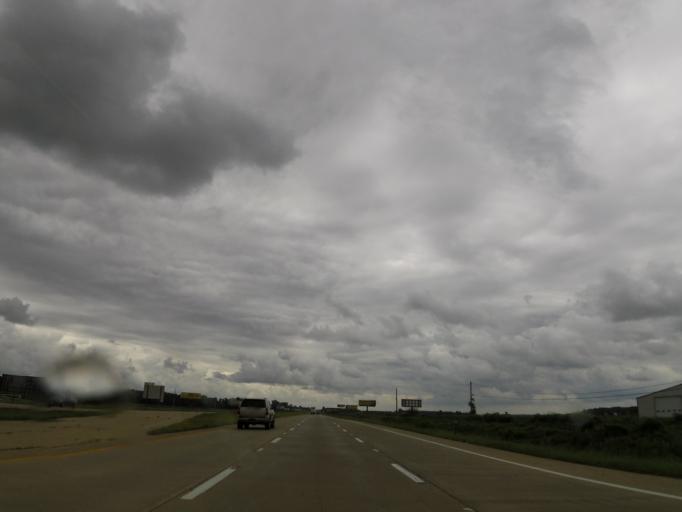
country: US
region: Missouri
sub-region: Mississippi County
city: Charleston
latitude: 36.9237
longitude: -89.3153
